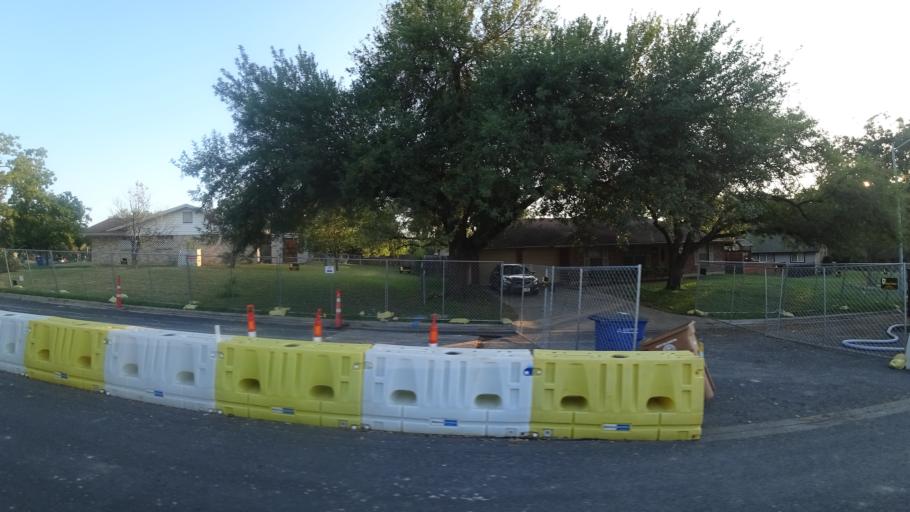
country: US
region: Texas
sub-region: Travis County
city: Austin
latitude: 30.3254
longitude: -97.6845
